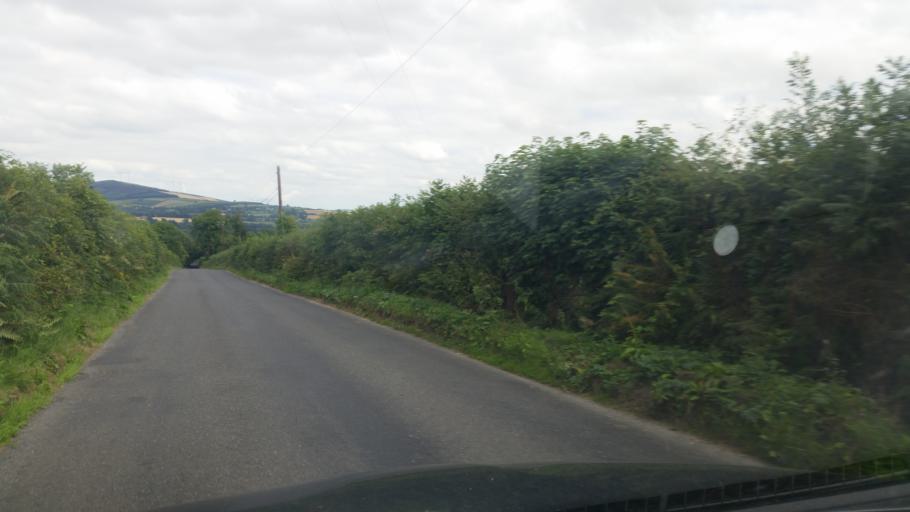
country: IE
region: Leinster
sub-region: Loch Garman
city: Bunclody
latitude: 52.6504
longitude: -6.6798
